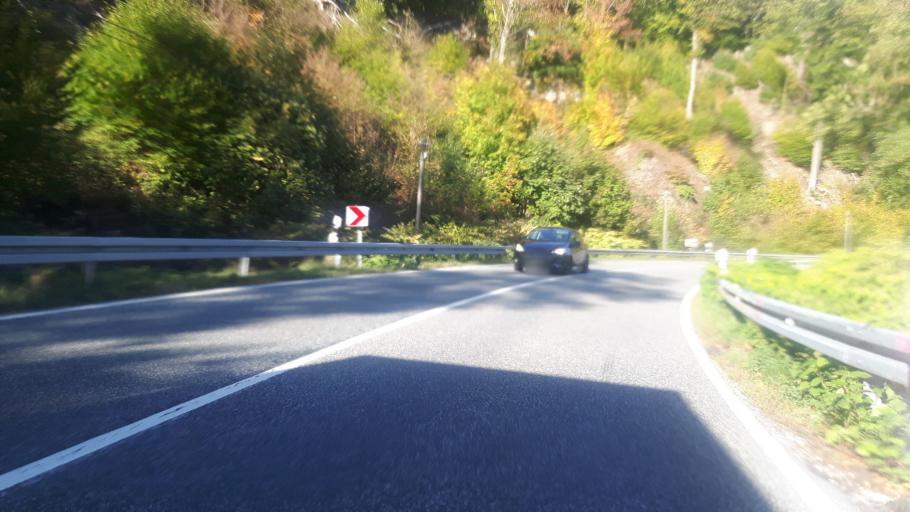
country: DE
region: Rheinland-Pfalz
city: Katzwinkel
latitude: 50.8013
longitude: 7.8147
